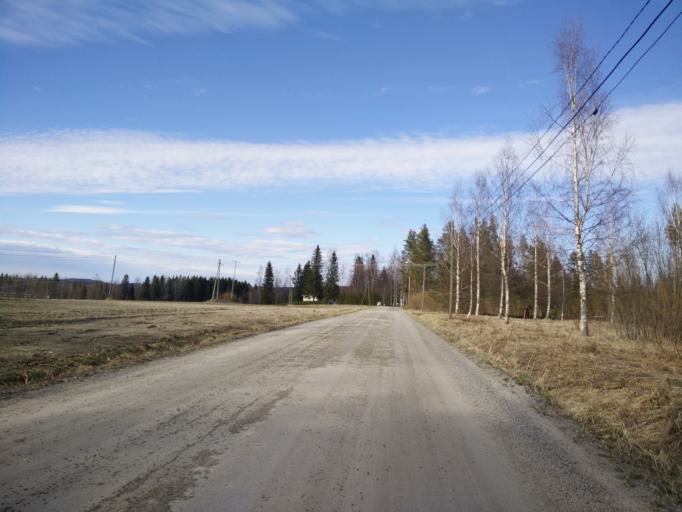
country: FI
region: Pirkanmaa
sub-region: Tampere
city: Orivesi
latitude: 61.6950
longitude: 24.3615
